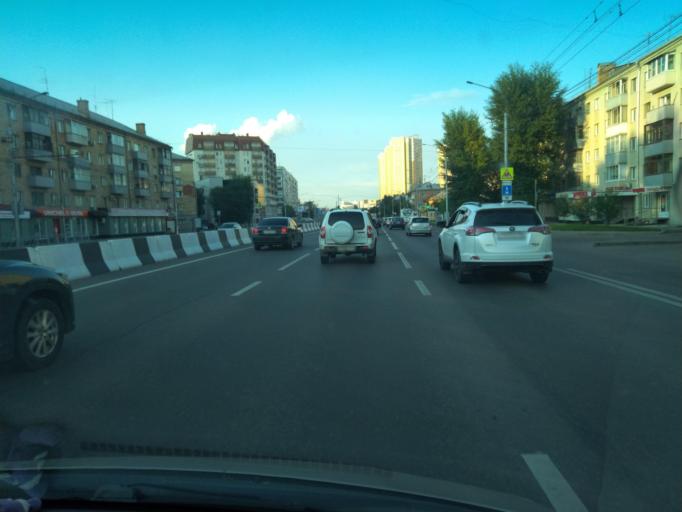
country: RU
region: Krasnoyarskiy
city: Krasnoyarsk
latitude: 56.0296
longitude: 92.9154
